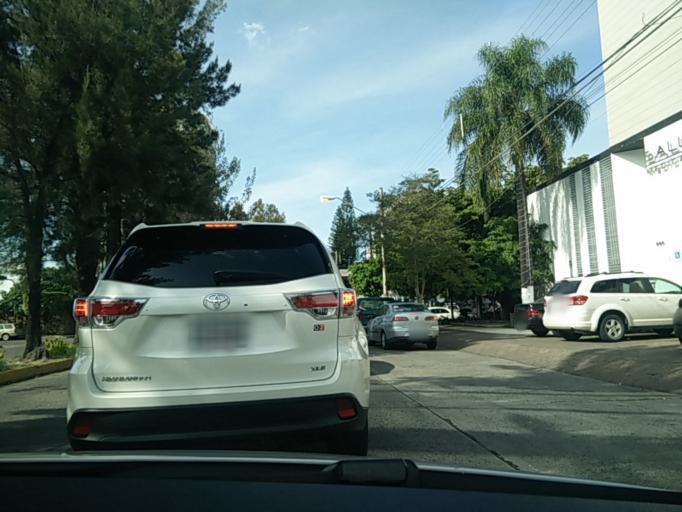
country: MX
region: Jalisco
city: Guadalajara
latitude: 20.6891
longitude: -103.3870
